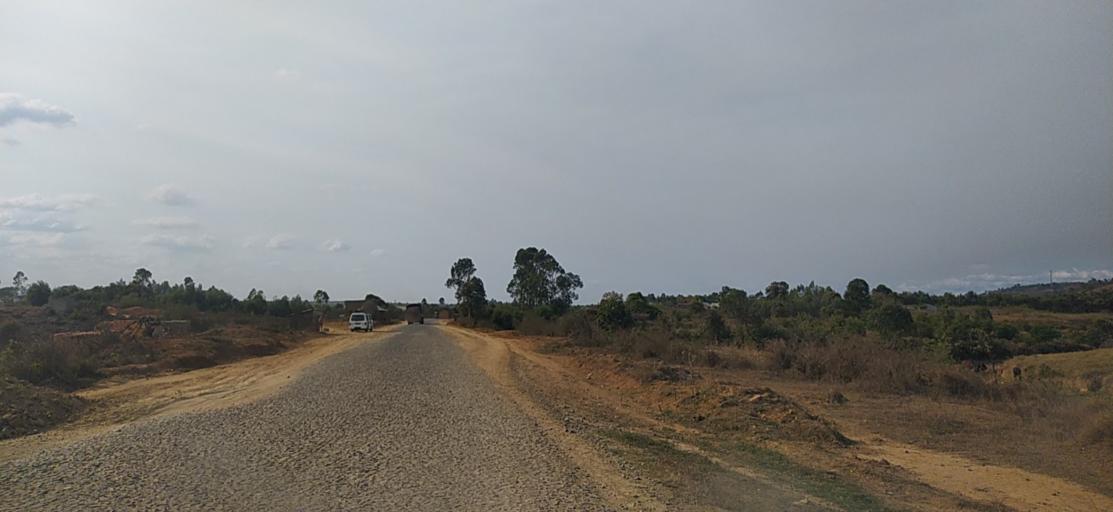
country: MG
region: Alaotra Mangoro
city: Moramanga
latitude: -18.6652
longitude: 48.2745
